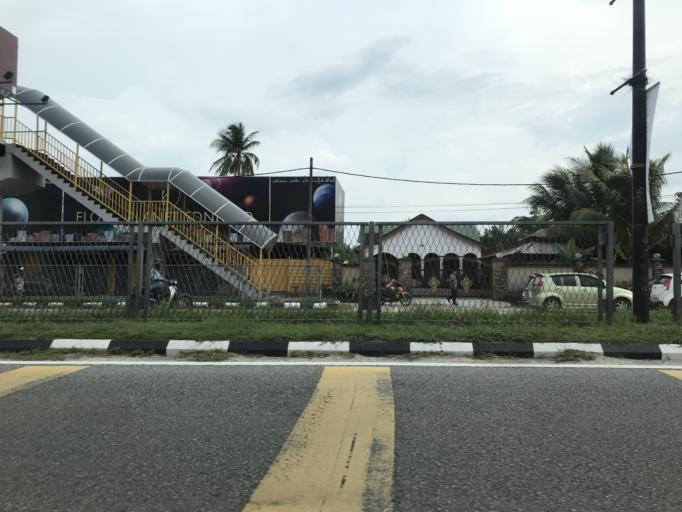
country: MY
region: Kelantan
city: Kota Bharu
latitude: 6.1183
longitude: 102.2200
